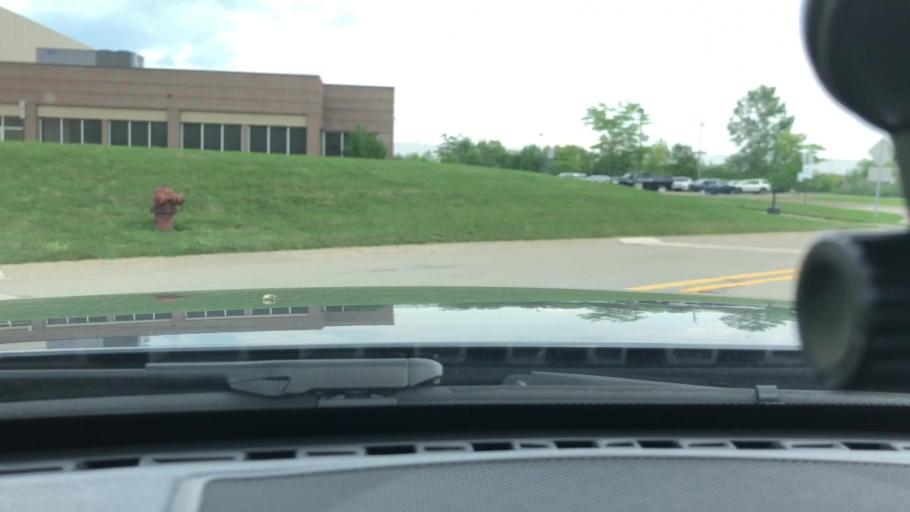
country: US
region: Michigan
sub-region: Wayne County
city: Livonia
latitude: 42.3748
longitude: -83.3402
